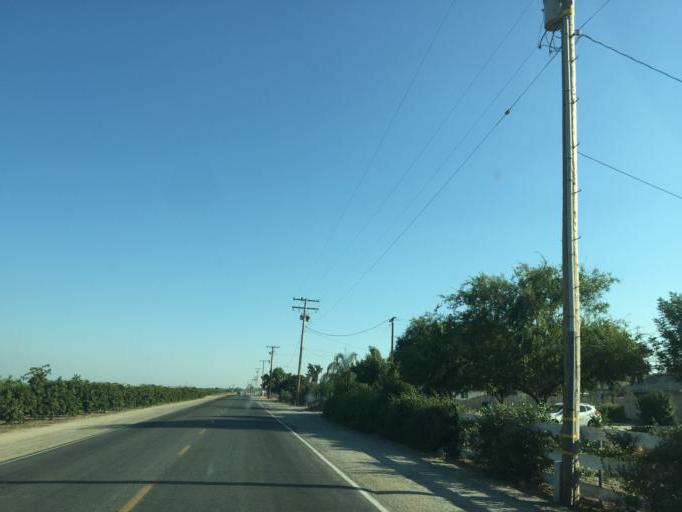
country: US
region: California
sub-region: Tulare County
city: Ivanhoe
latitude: 36.4234
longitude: -119.2780
